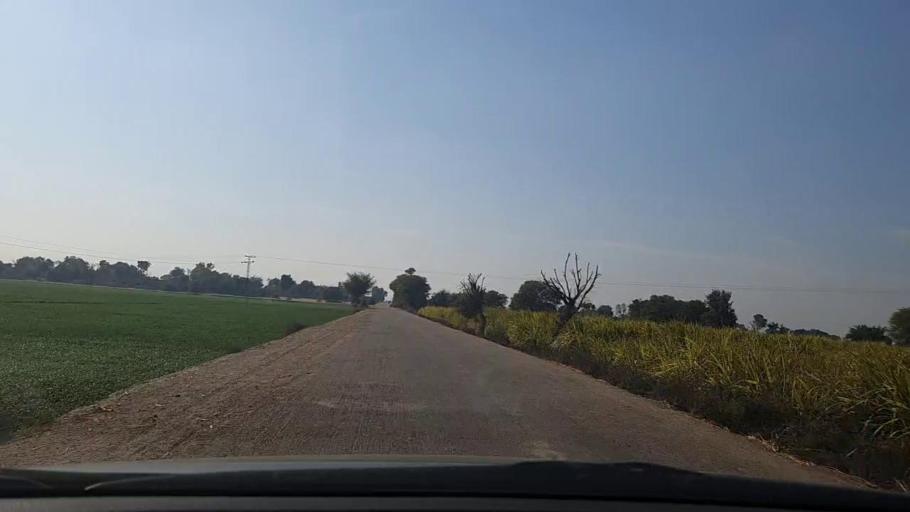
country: PK
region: Sindh
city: Daulatpur
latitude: 26.3212
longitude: 68.0233
